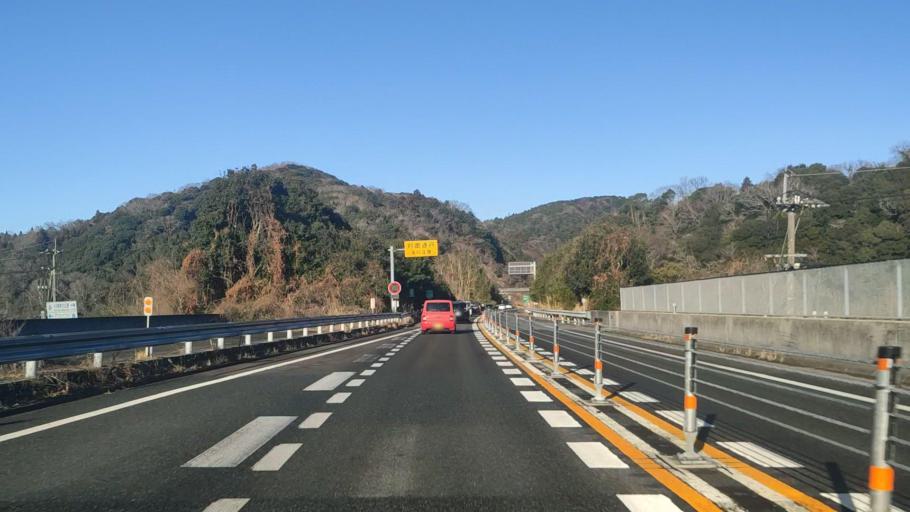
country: JP
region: Oita
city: Bungo-Takada-shi
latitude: 33.4467
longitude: 131.3673
